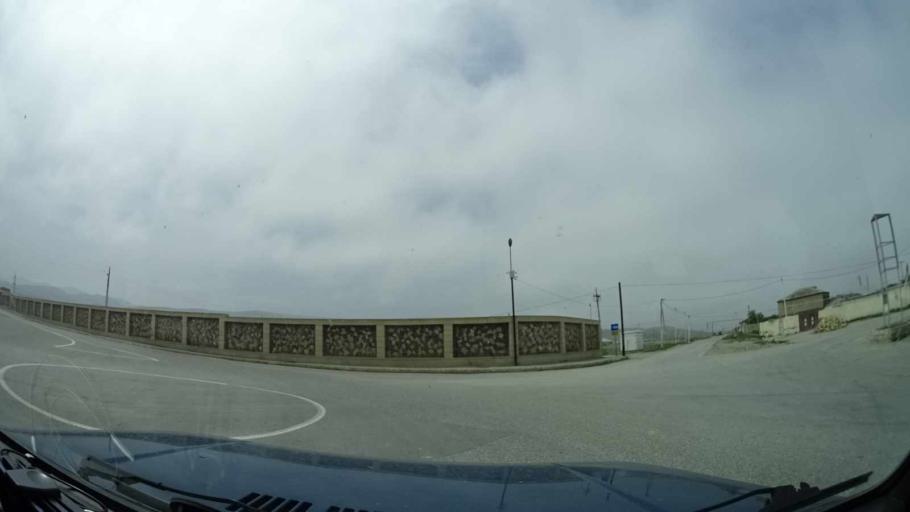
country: AZ
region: Xizi
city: Kilyazi
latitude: 40.8688
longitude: 49.3407
